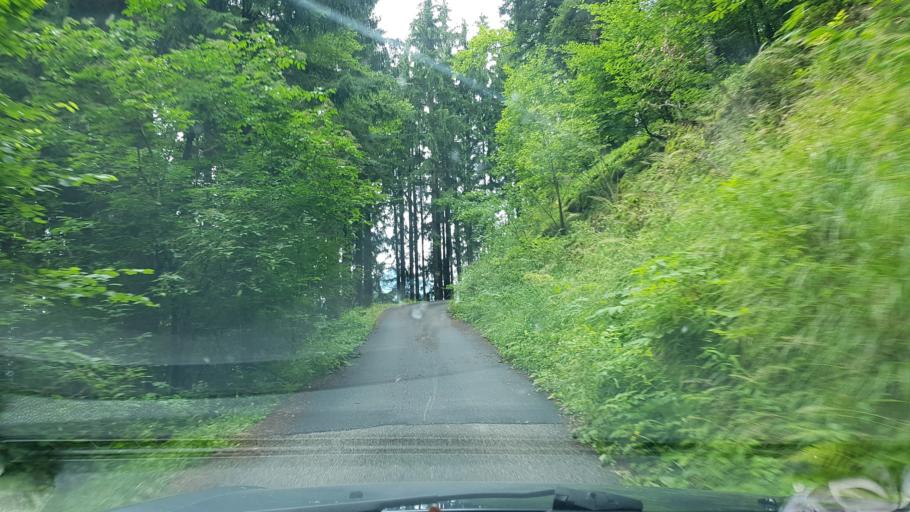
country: IT
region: Friuli Venezia Giulia
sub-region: Provincia di Udine
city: Cercivento
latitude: 46.5362
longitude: 12.9863
